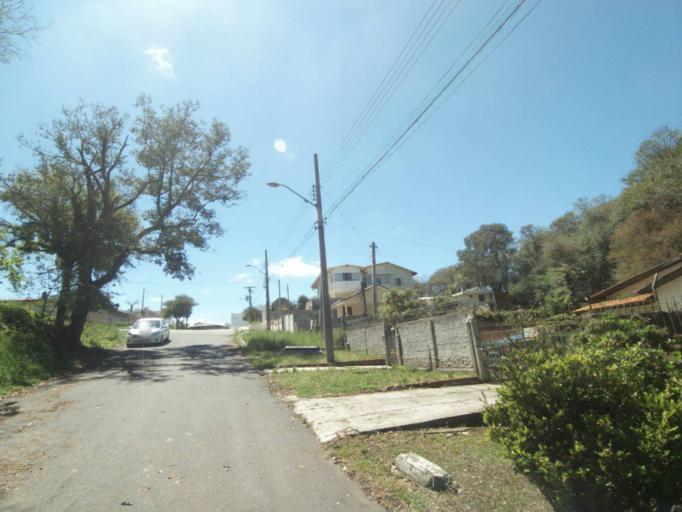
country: BR
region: Parana
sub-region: Curitiba
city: Curitiba
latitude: -25.3861
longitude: -49.2663
